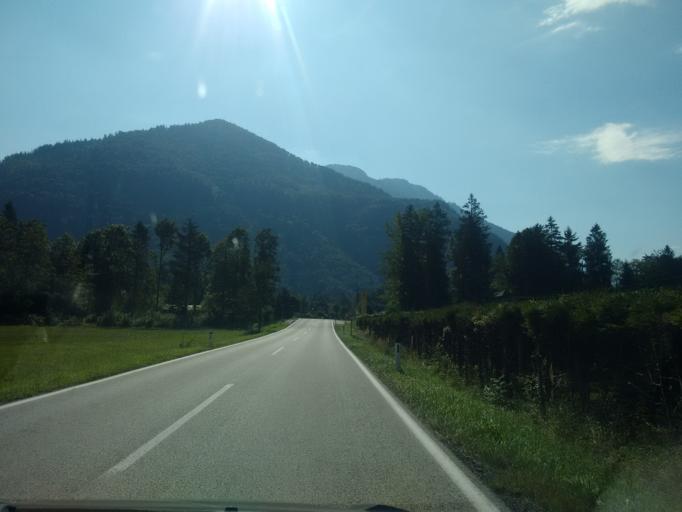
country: AT
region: Upper Austria
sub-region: Politischer Bezirk Gmunden
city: Gruenau im Almtal
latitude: 47.8358
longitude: 13.9500
